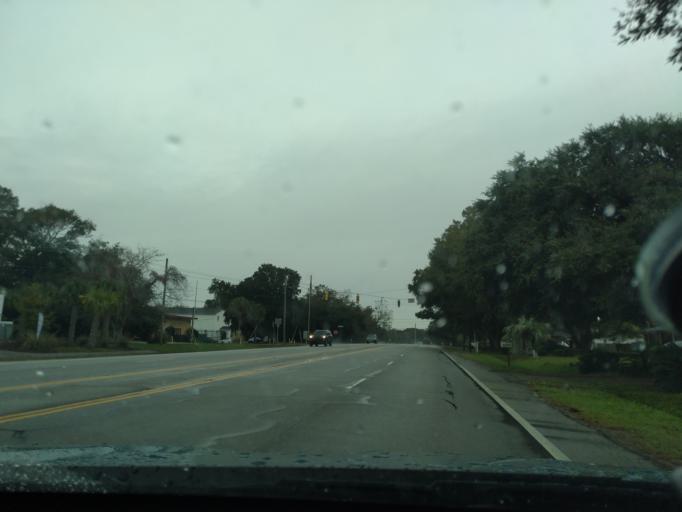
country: US
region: South Carolina
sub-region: Charleston County
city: Folly Beach
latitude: 32.6929
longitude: -79.9647
